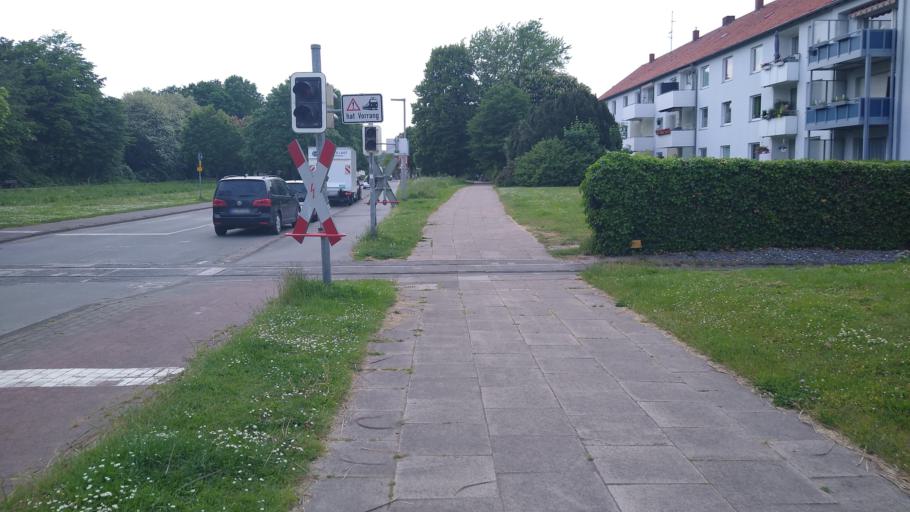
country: DE
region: North Rhine-Westphalia
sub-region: Regierungsbezirk Detmold
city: Bielefeld
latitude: 52.0101
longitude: 8.5606
